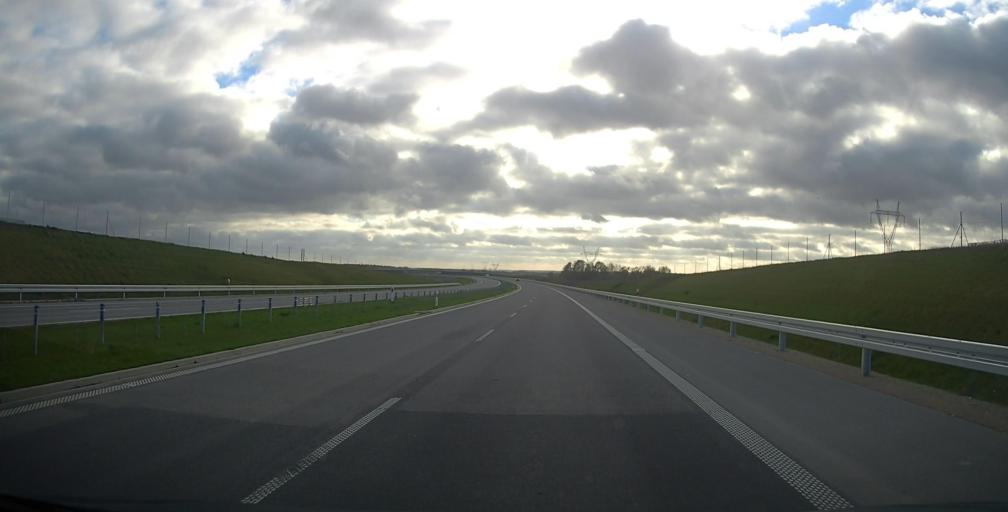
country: PL
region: Podlasie
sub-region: Powiat grajewski
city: Szczuczyn
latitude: 53.6447
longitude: 22.2930
